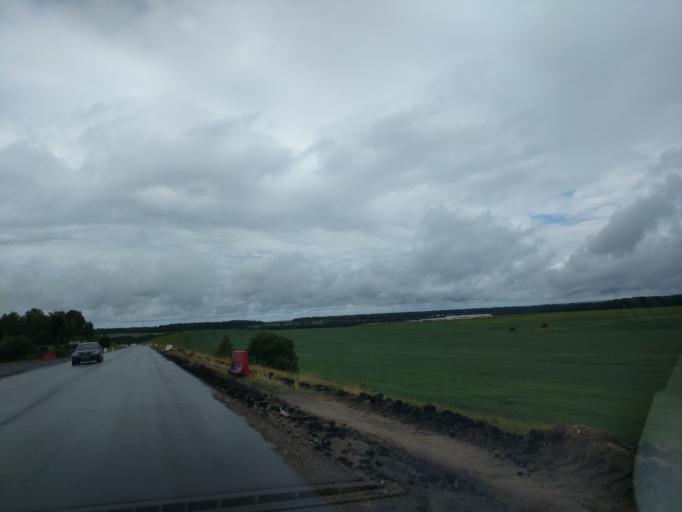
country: BY
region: Minsk
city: Il'ya
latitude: 54.2873
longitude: 27.4864
